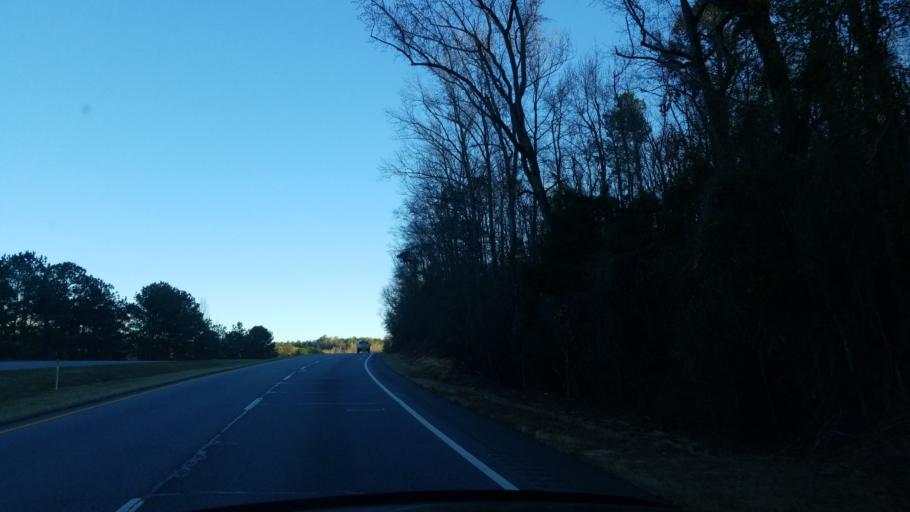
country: US
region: Georgia
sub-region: Chattahoochee County
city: Cusseta
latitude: 32.2625
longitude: -84.7339
